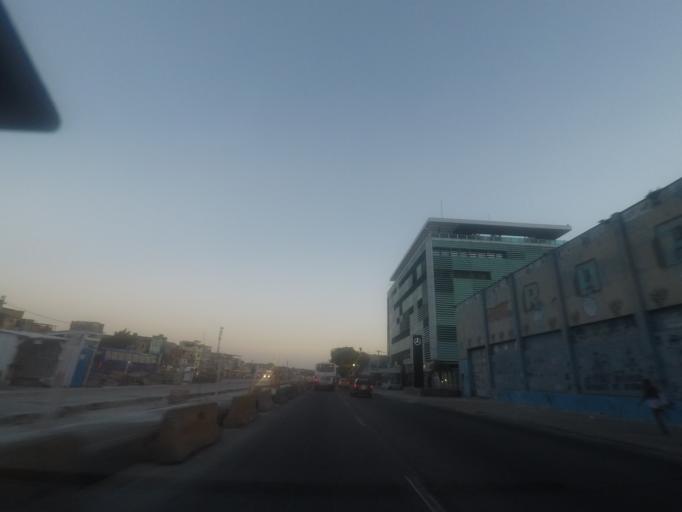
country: BR
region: Rio de Janeiro
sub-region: Rio De Janeiro
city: Rio de Janeiro
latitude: -22.8406
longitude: -43.2534
